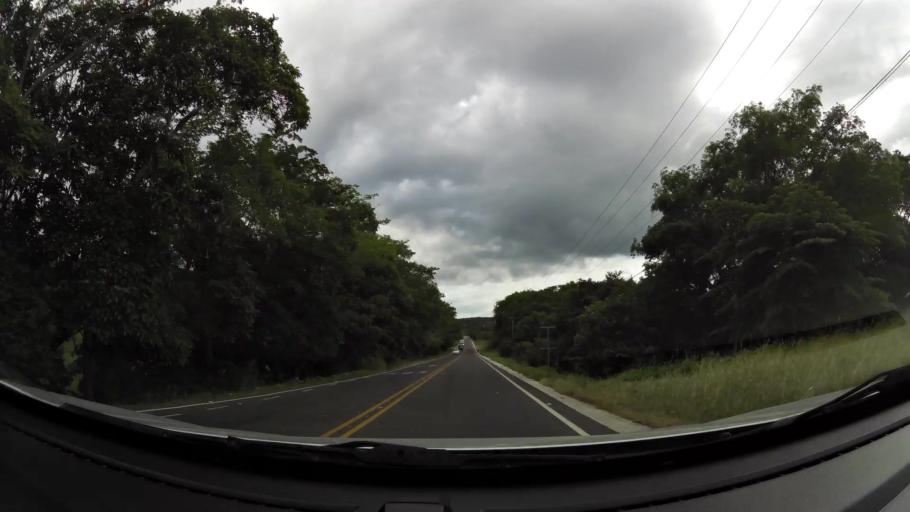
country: CR
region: Guanacaste
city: Nandayure
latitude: 10.2494
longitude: -85.2278
